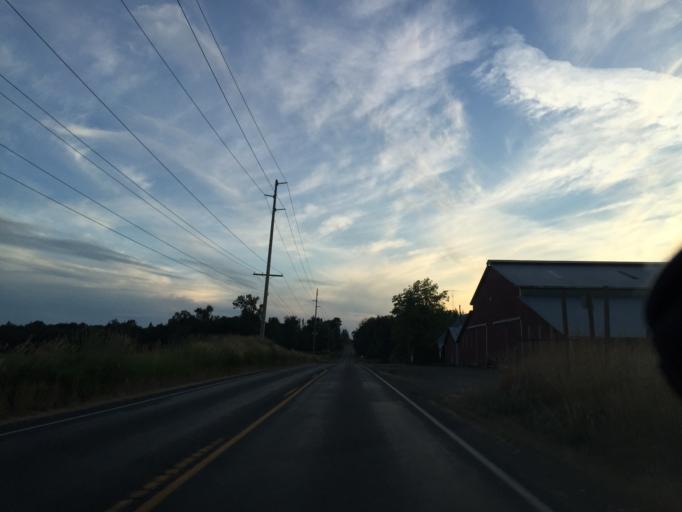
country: US
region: Washington
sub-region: Whatcom County
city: Everson
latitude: 48.9639
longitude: -122.3892
